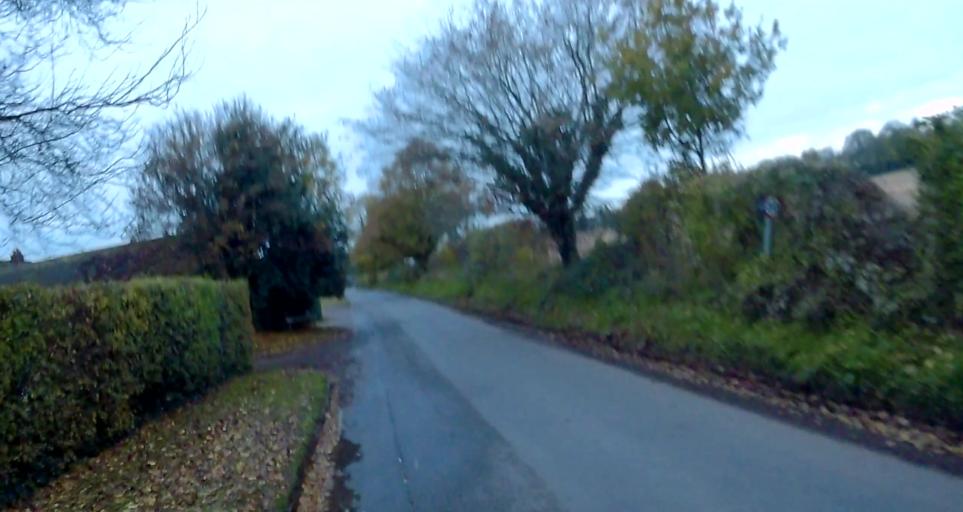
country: GB
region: England
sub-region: Hampshire
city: Old Basing
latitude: 51.2314
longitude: -0.9960
